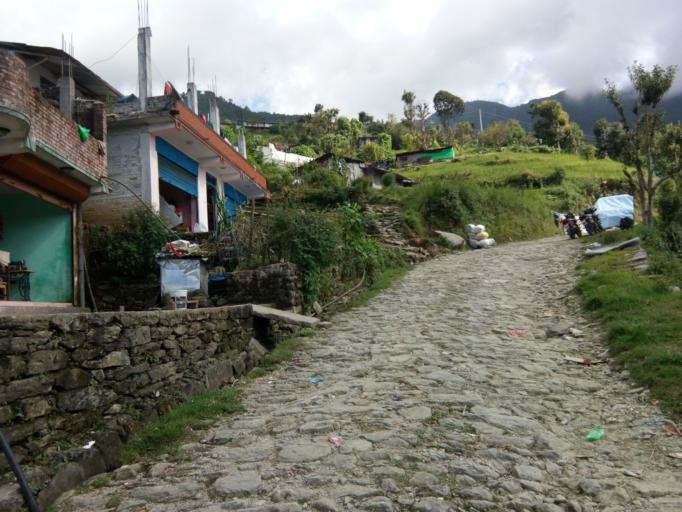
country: NP
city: Kodari
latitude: 27.7036
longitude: 85.9210
